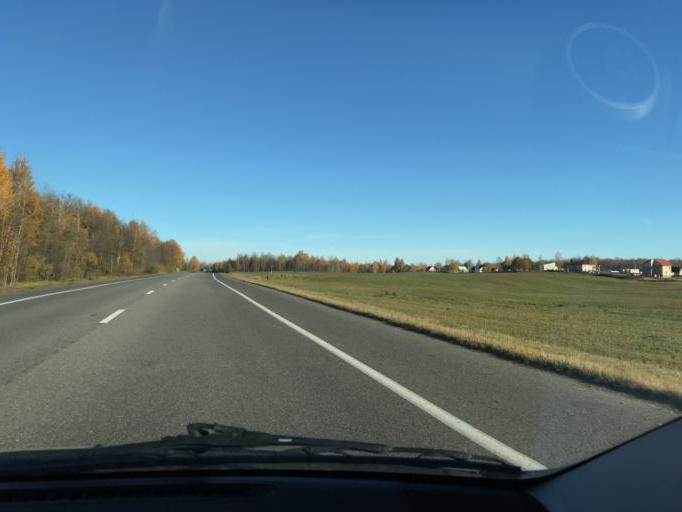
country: BY
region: Vitebsk
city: Vitebsk
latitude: 55.0760
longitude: 30.3080
